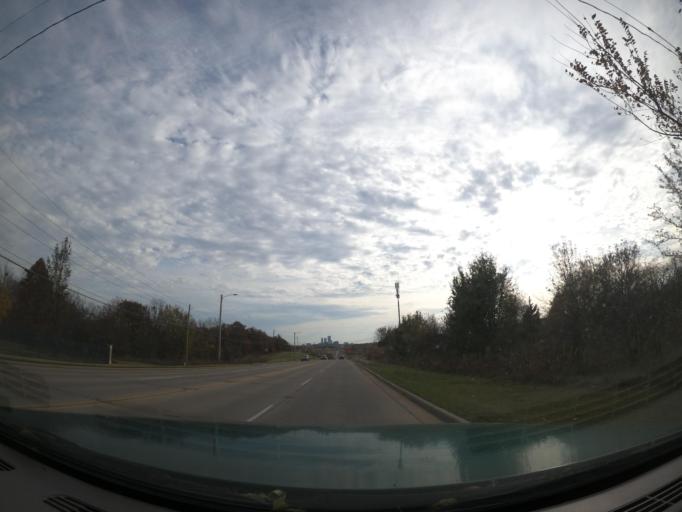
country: US
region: Oklahoma
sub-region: Tulsa County
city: Turley
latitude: 36.2085
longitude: -95.9936
